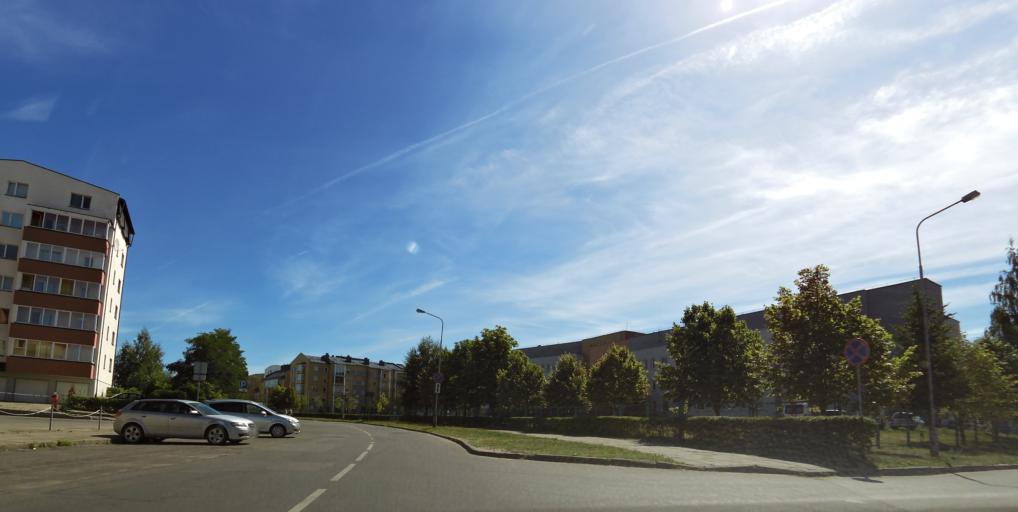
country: LT
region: Vilnius County
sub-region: Vilnius
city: Fabijoniskes
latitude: 54.7231
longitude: 25.2363
